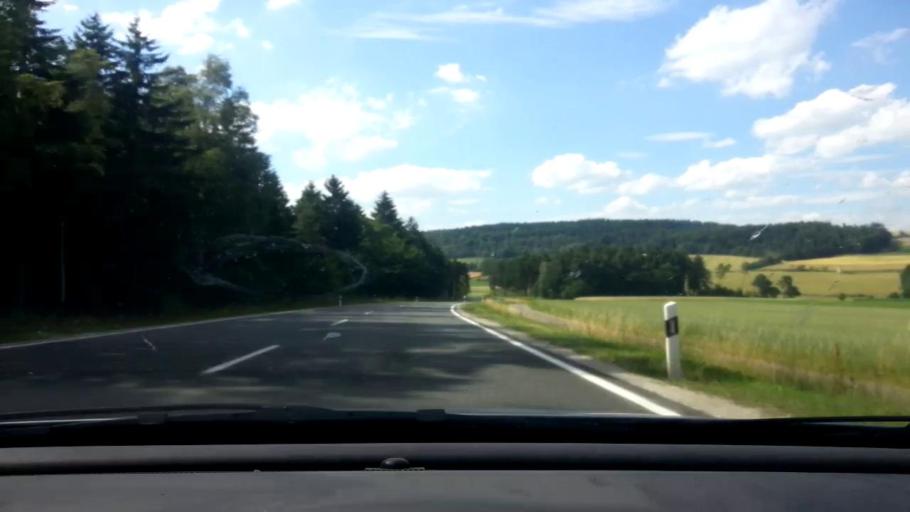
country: DE
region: Bavaria
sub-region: Upper Palatinate
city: Erbendorf
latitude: 49.8456
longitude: 11.9993
